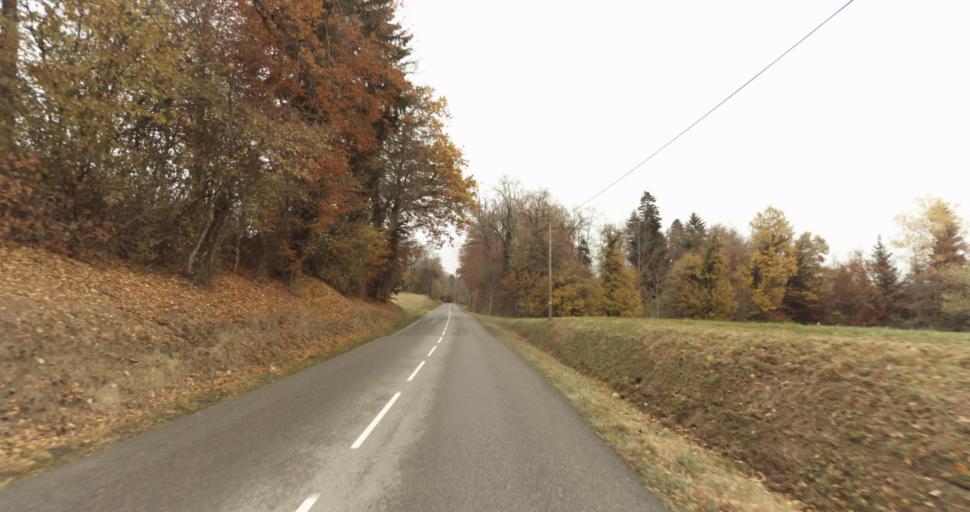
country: FR
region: Rhone-Alpes
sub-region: Departement de la Haute-Savoie
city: Evires
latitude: 46.0340
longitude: 6.2089
